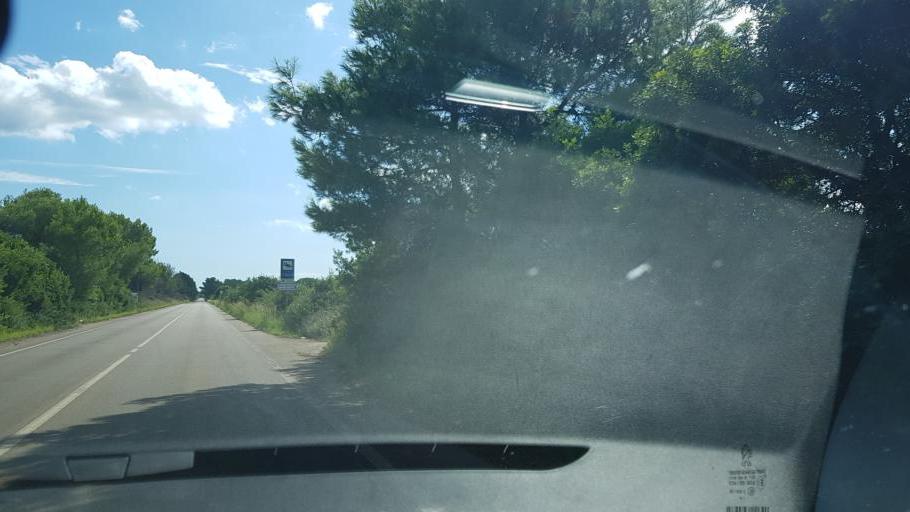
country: IT
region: Apulia
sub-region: Provincia di Lecce
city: Borgagne
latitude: 40.2520
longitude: 18.4394
